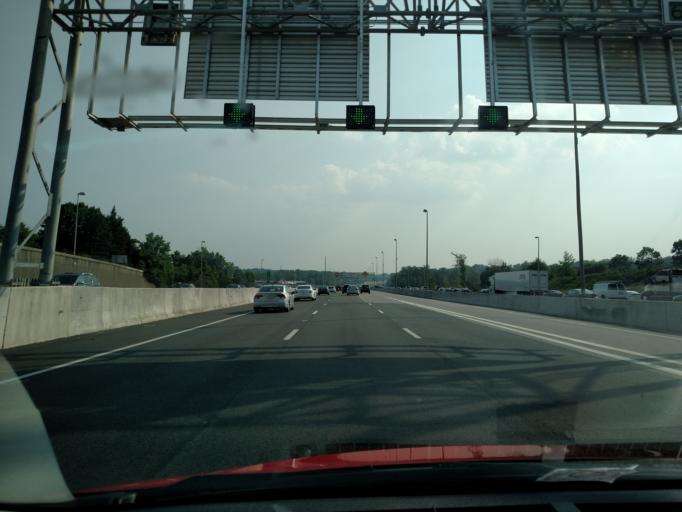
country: US
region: Virginia
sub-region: Fairfax County
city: Newington
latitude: 38.7325
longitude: -77.1961
